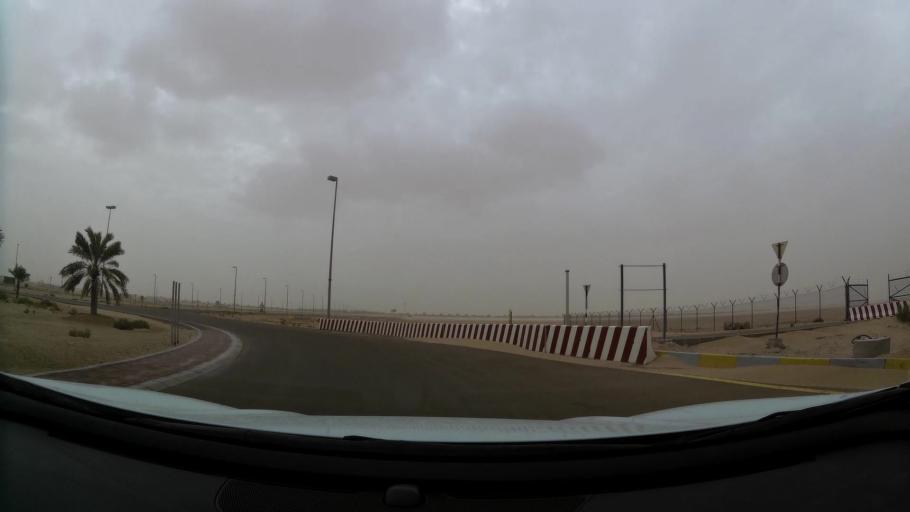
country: AE
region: Abu Dhabi
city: Abu Dhabi
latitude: 24.4235
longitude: 54.6951
